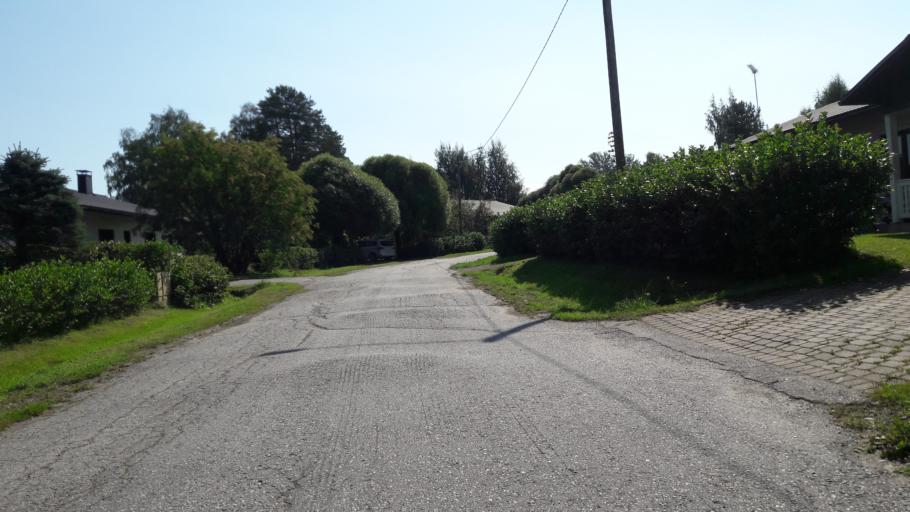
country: FI
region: North Karelia
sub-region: Joensuu
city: Joensuu
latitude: 62.5324
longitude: 29.8369
